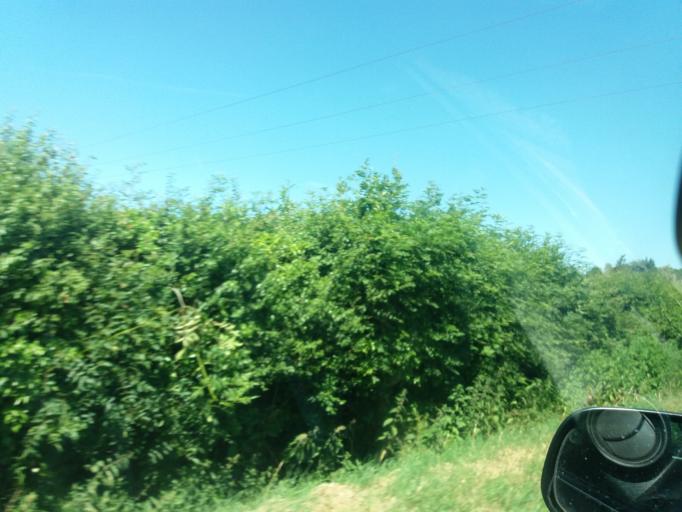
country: IE
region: Leinster
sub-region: Fingal County
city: Swords
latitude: 53.4638
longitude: -6.2722
